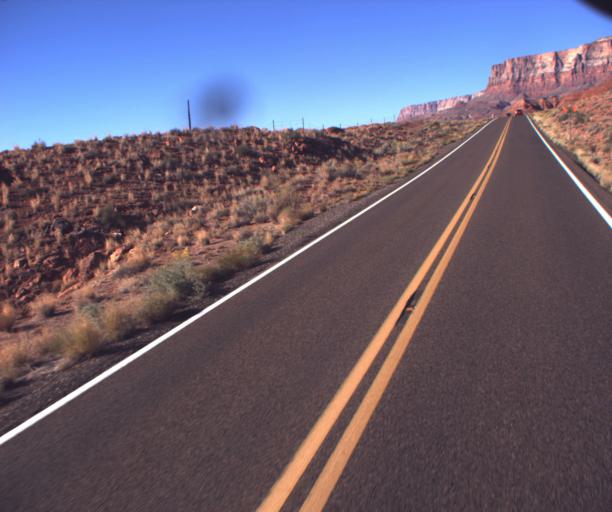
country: US
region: Arizona
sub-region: Coconino County
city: Page
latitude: 36.8087
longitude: -111.6653
